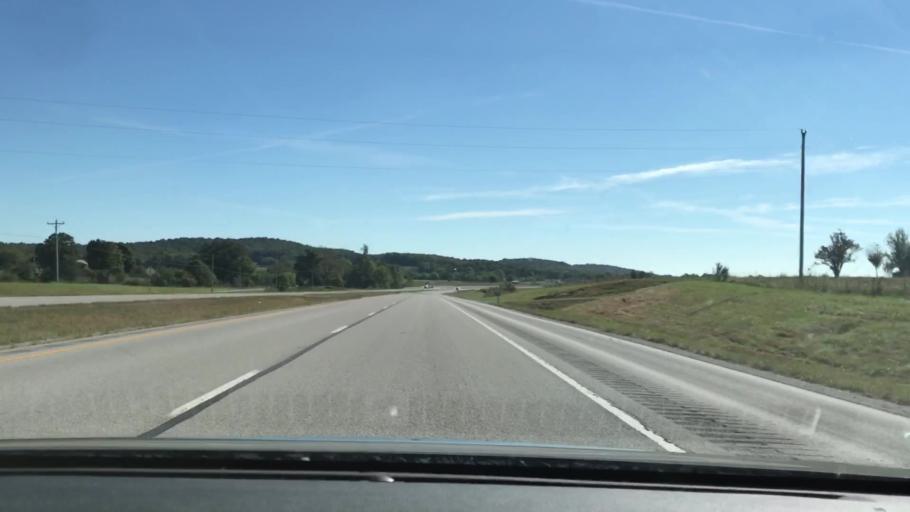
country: US
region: Kentucky
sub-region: Todd County
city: Elkton
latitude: 36.8401
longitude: -87.2514
